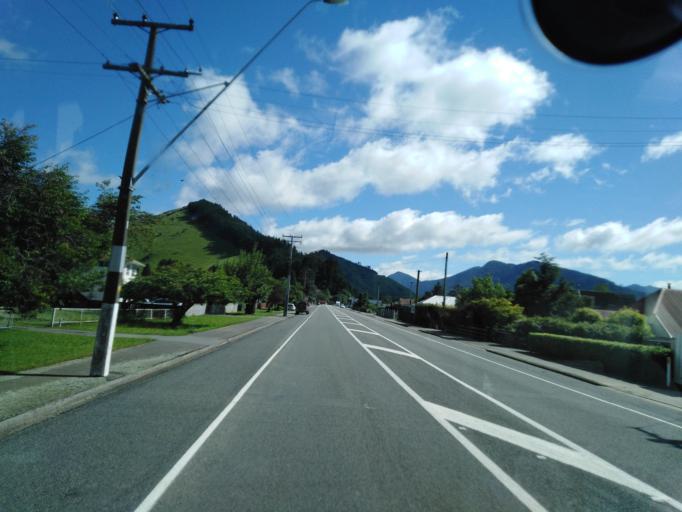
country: NZ
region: Nelson
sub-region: Nelson City
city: Nelson
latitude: -41.2305
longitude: 173.5822
